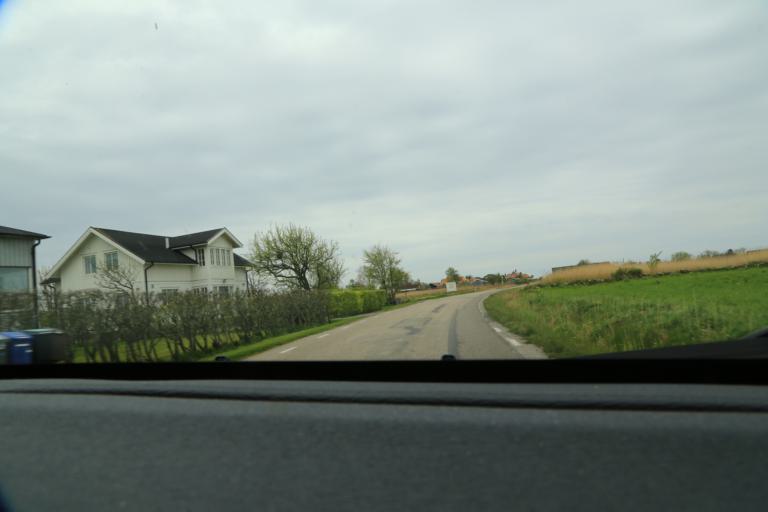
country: SE
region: Halland
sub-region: Varbergs Kommun
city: Traslovslage
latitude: 57.0302
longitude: 12.3237
